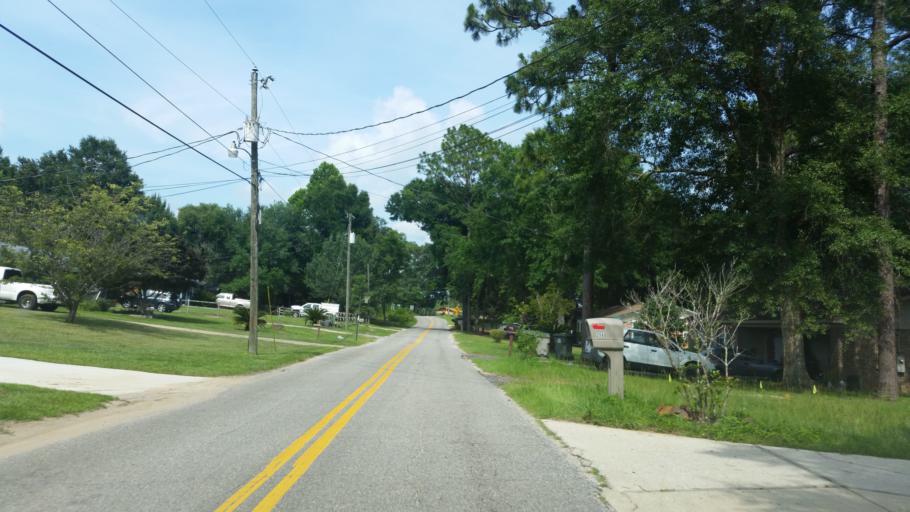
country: US
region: Florida
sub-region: Escambia County
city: Cantonment
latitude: 30.5687
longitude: -87.3644
